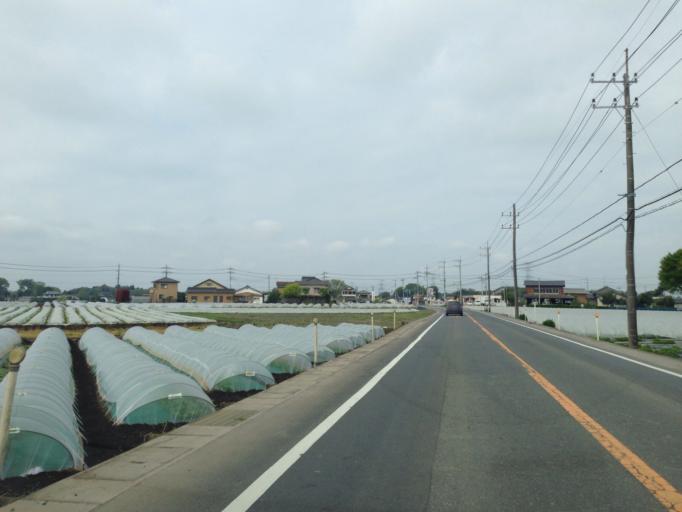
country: JP
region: Ibaraki
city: Ishige
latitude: 36.1622
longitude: 139.9108
